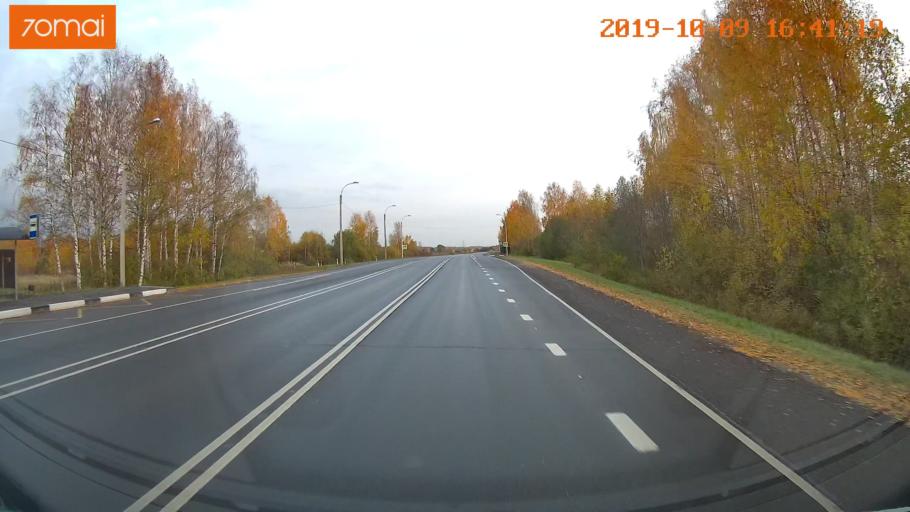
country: RU
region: Kostroma
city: Volgorechensk
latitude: 57.4741
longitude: 41.0787
